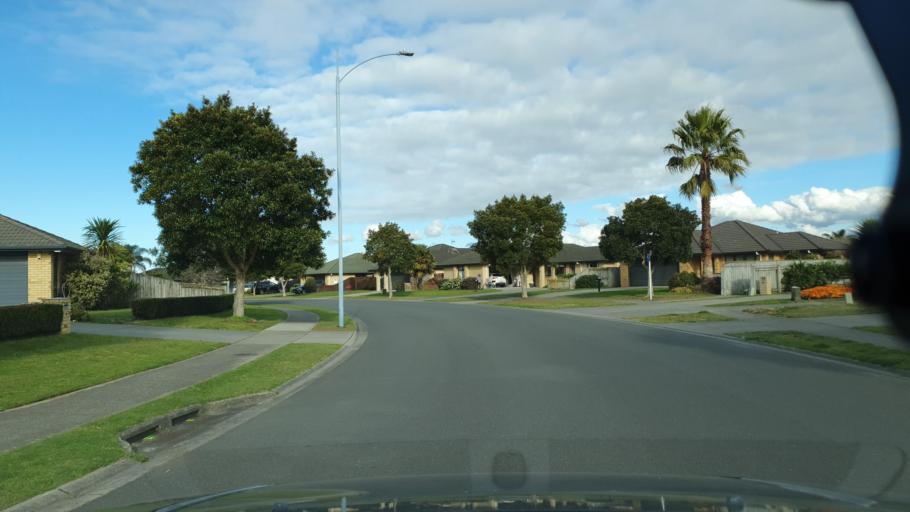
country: NZ
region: Bay of Plenty
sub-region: Tauranga City
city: Tauranga
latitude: -37.7090
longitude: 176.2910
